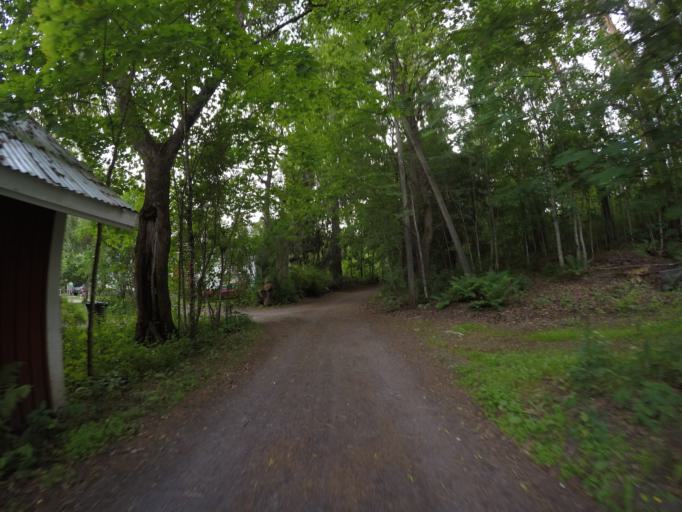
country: FI
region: Haeme
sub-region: Haemeenlinna
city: Haemeenlinna
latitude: 60.9736
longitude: 24.4353
